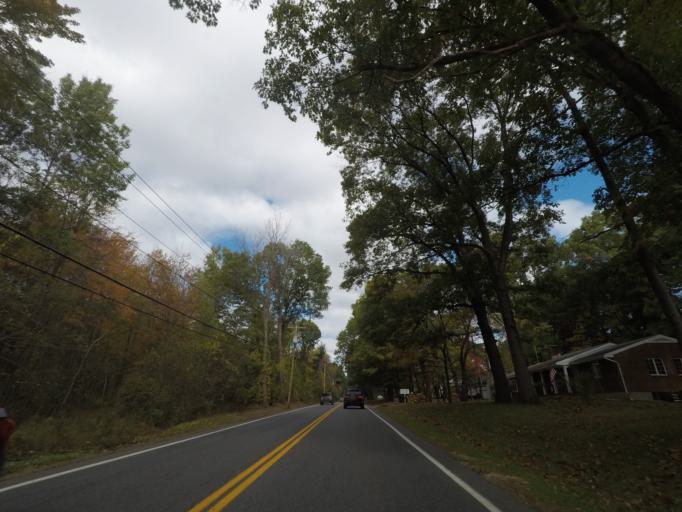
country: US
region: New York
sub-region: Saratoga County
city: Country Knolls
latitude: 42.8456
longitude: -73.7698
